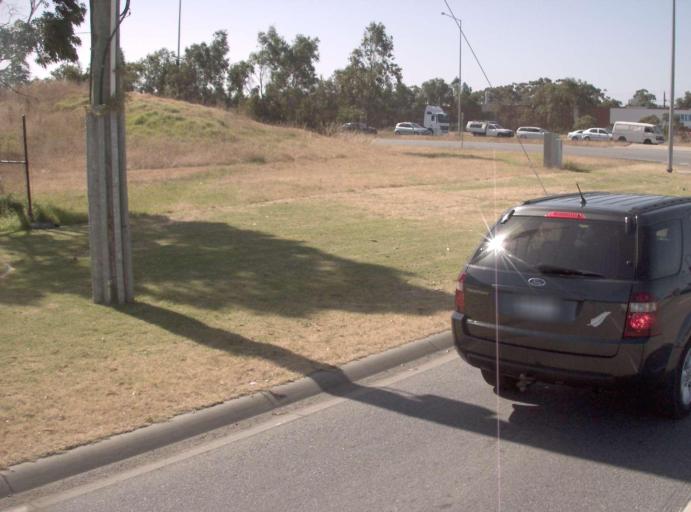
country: AU
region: Victoria
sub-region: Casey
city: Doveton
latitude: -38.0047
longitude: 145.2172
